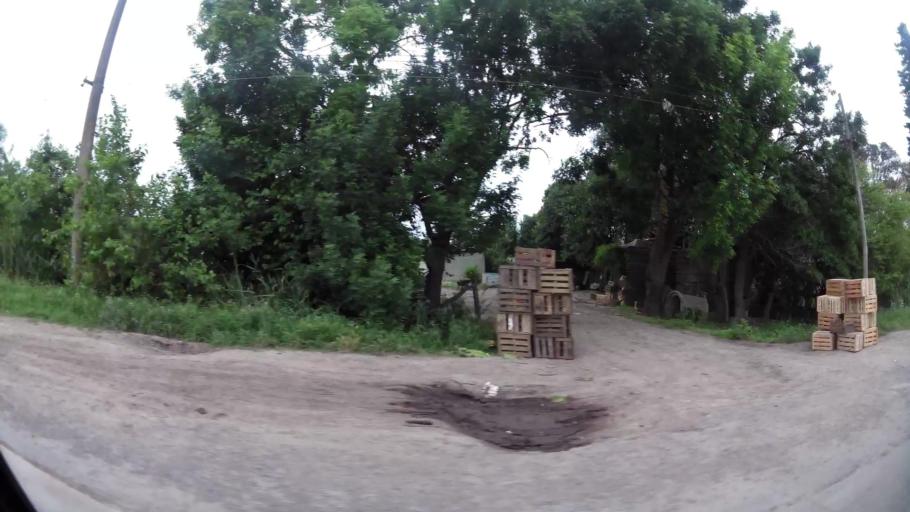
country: AR
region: Buenos Aires
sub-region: Partido de La Plata
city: La Plata
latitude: -35.0286
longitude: -58.0847
